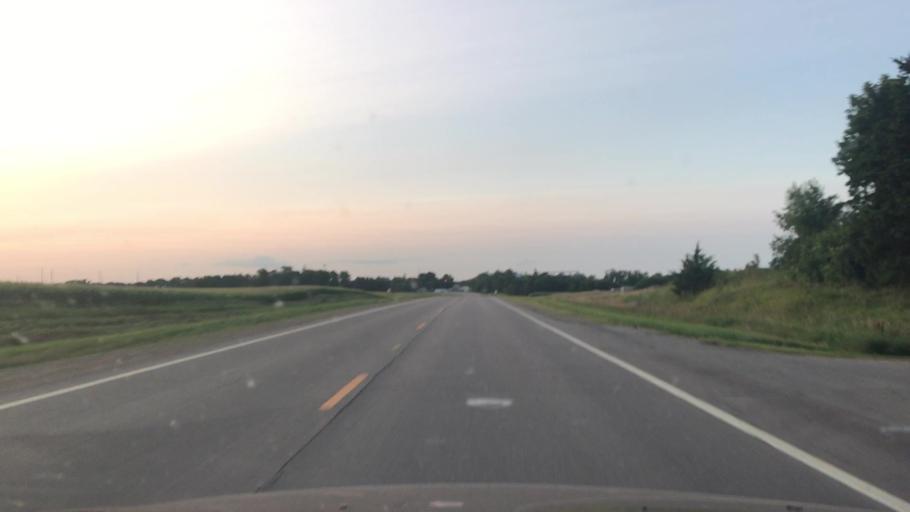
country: US
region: Minnesota
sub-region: Redwood County
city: Redwood Falls
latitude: 44.5184
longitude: -95.1181
